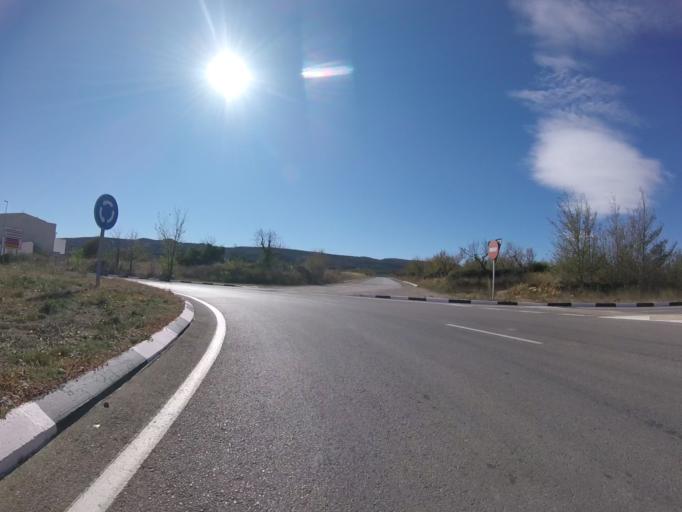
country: ES
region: Valencia
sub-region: Provincia de Castello
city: Albocasser
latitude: 40.3580
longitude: 0.0180
